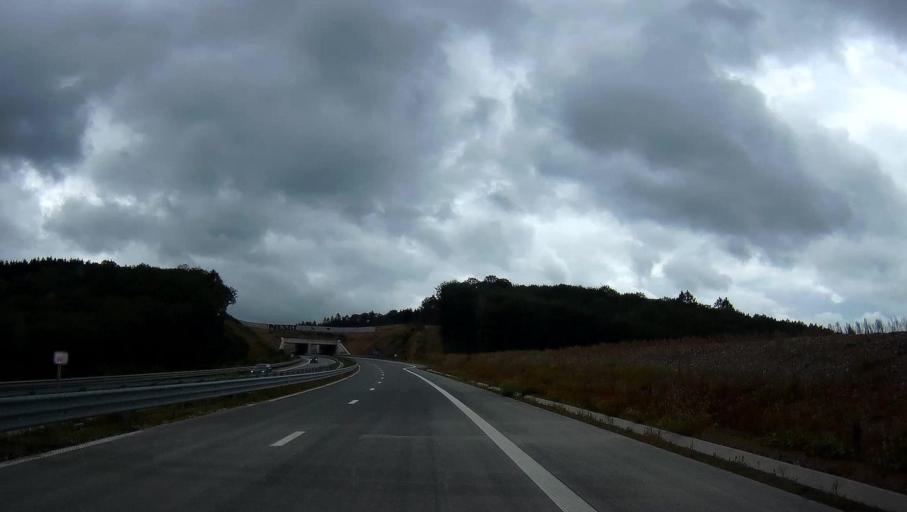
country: BE
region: Wallonia
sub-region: Province de Namur
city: Couvin
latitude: 50.0355
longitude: 4.5073
